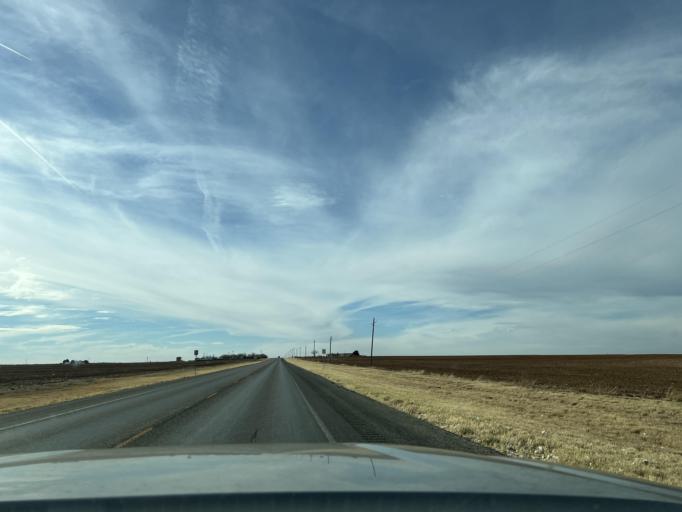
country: US
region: Texas
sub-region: Jones County
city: Anson
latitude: 32.7518
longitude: -99.9101
